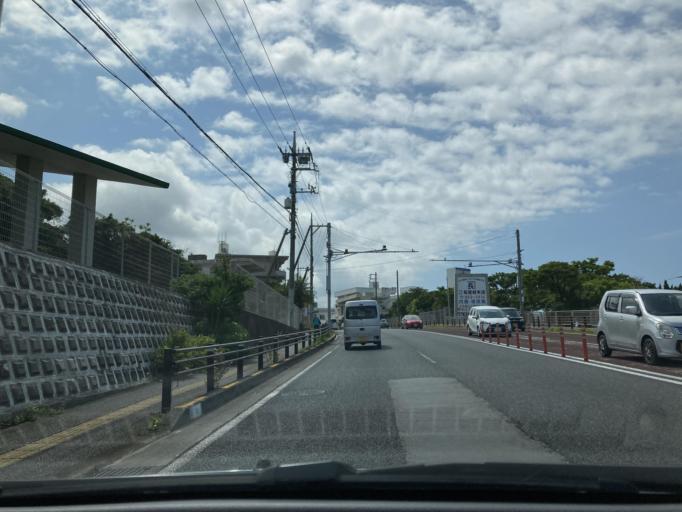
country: JP
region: Okinawa
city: Chatan
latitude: 26.2863
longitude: 127.7768
